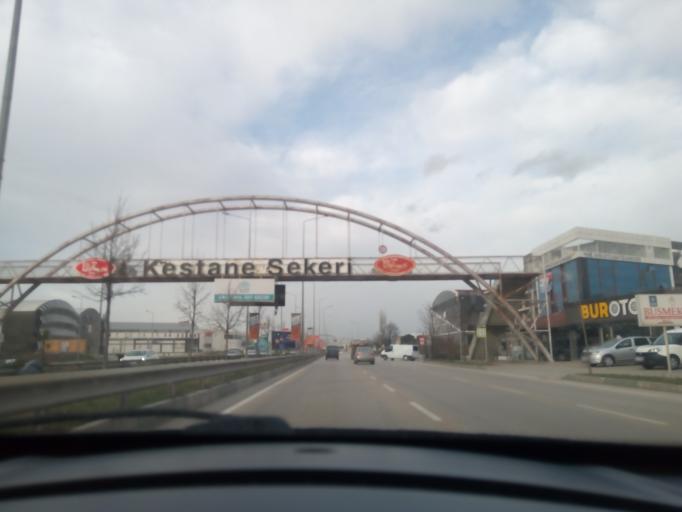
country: TR
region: Bursa
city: Cali
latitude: 40.2131
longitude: 28.9232
